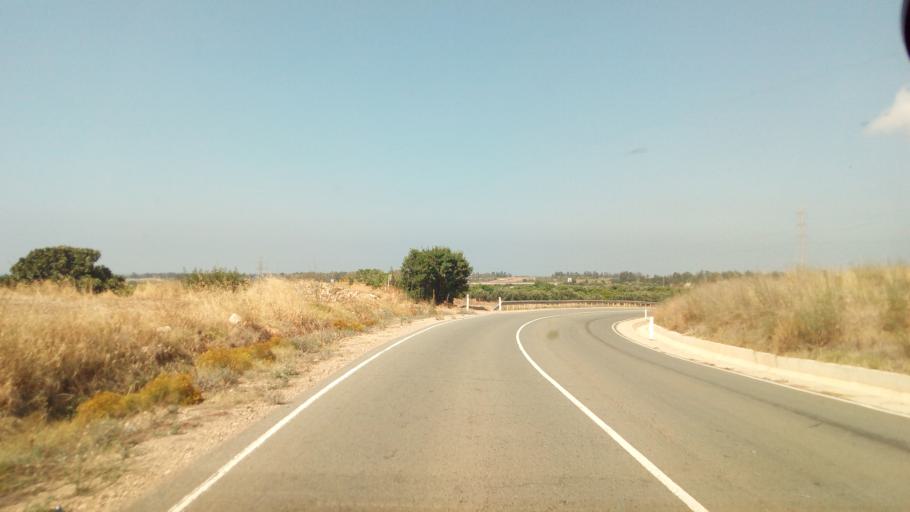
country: CY
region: Pafos
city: Mesogi
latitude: 34.7166
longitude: 32.5552
